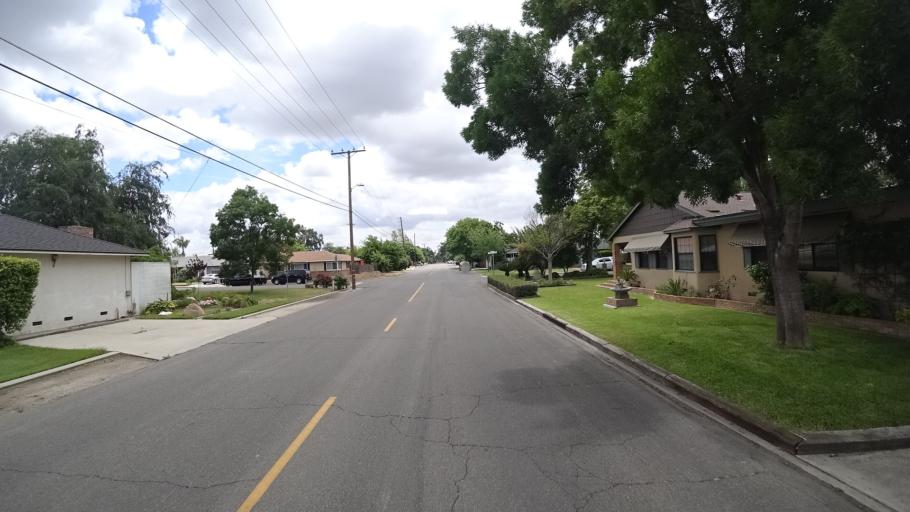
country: US
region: California
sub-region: Kings County
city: Hanford
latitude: 36.3472
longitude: -119.6483
